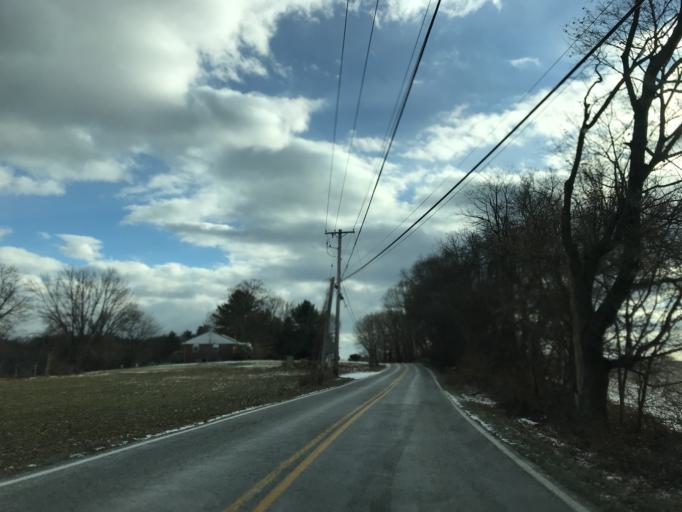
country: US
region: Maryland
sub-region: Harford County
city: Jarrettsville
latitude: 39.6102
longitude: -76.4427
